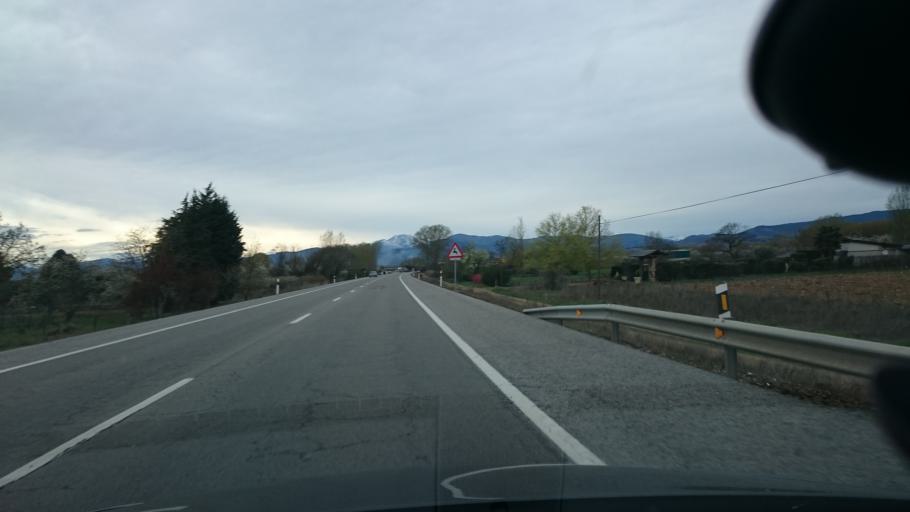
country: ES
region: Castille and Leon
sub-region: Provincia de Leon
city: Camponaraya
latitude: 42.5654
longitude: -6.6773
